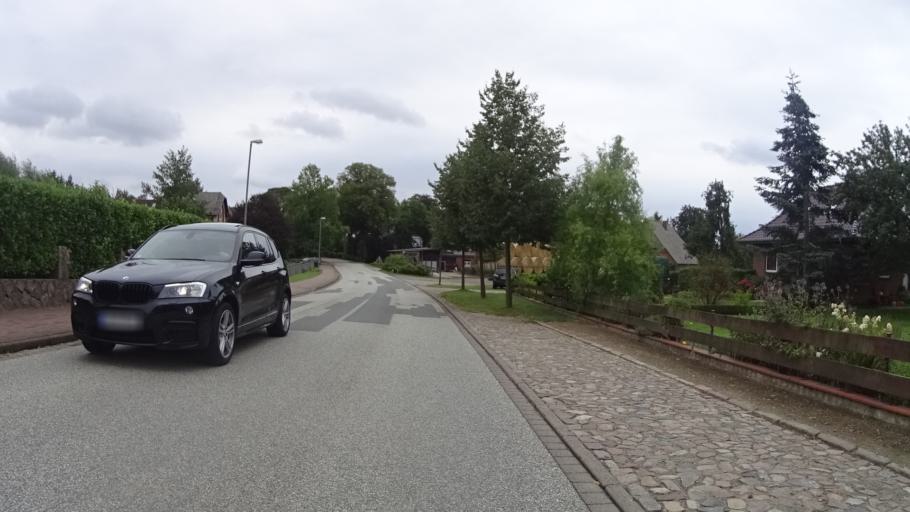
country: DE
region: Schleswig-Holstein
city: Klinkrade
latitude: 53.7143
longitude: 10.5545
